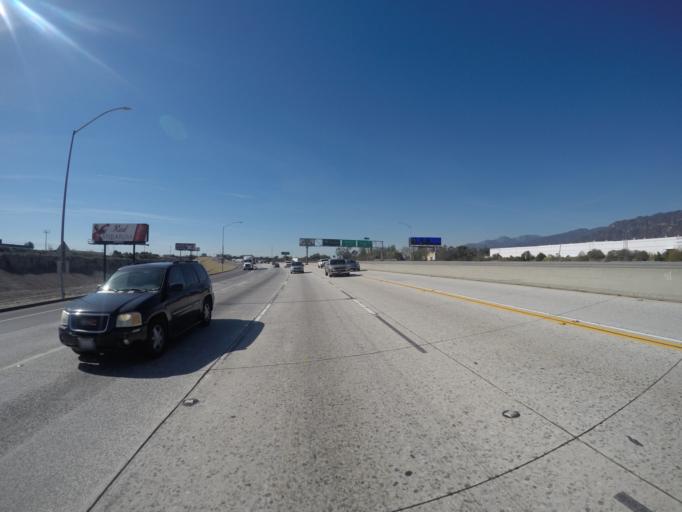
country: US
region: California
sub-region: Los Angeles County
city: Azusa
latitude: 34.1308
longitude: -117.9292
